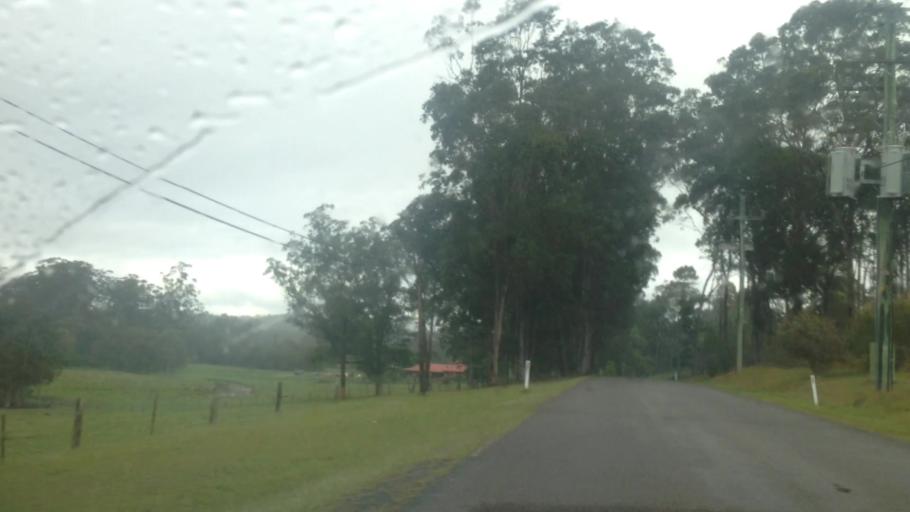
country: AU
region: New South Wales
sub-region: Wyong Shire
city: Little Jilliby
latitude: -33.2079
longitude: 151.3684
